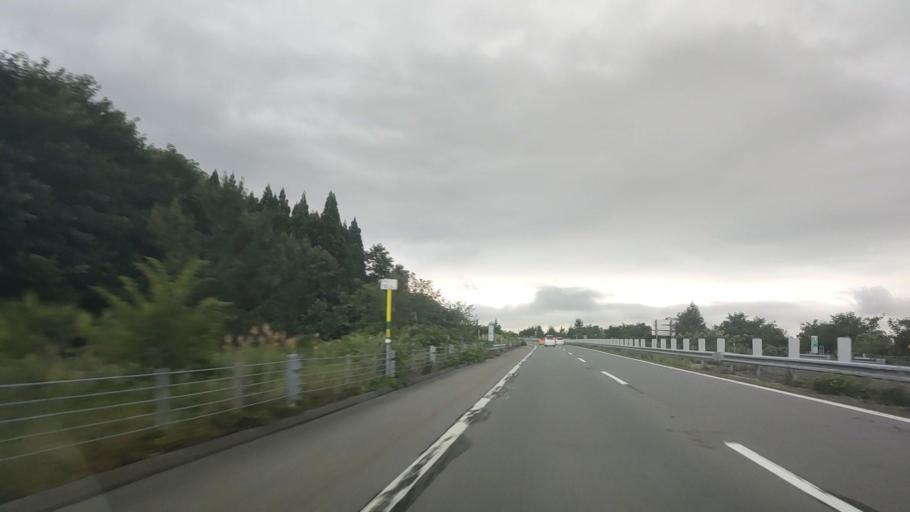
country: JP
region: Hokkaido
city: Nanae
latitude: 41.9059
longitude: 140.6973
